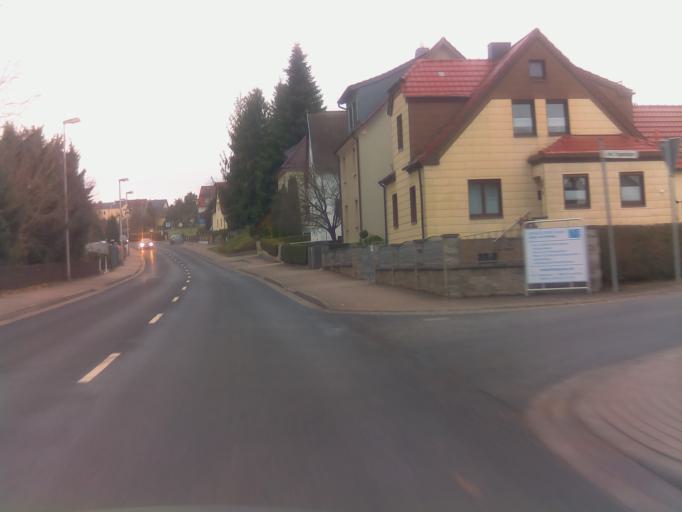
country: DE
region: Thuringia
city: Unterbreizbach
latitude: 50.7946
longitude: 9.9985
